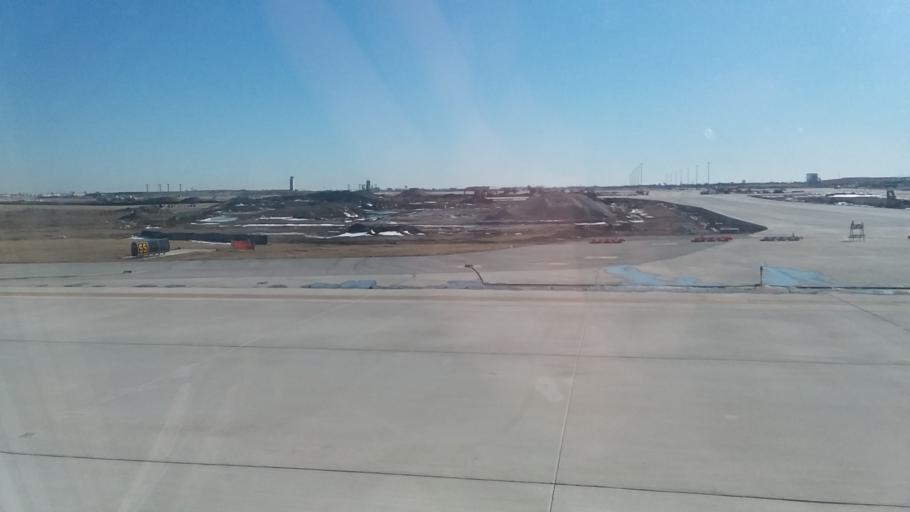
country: US
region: Illinois
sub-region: DuPage County
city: Bensenville
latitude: 41.9867
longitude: -87.9298
